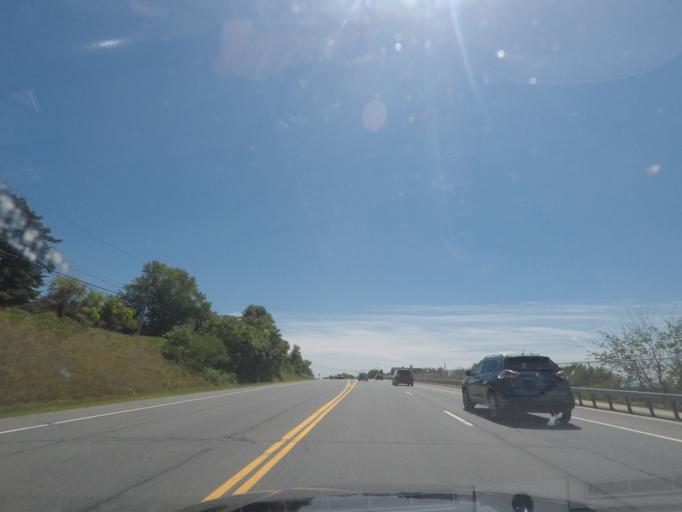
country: US
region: New York
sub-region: Rensselaer County
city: Hampton Manor
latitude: 42.6347
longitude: -73.7012
